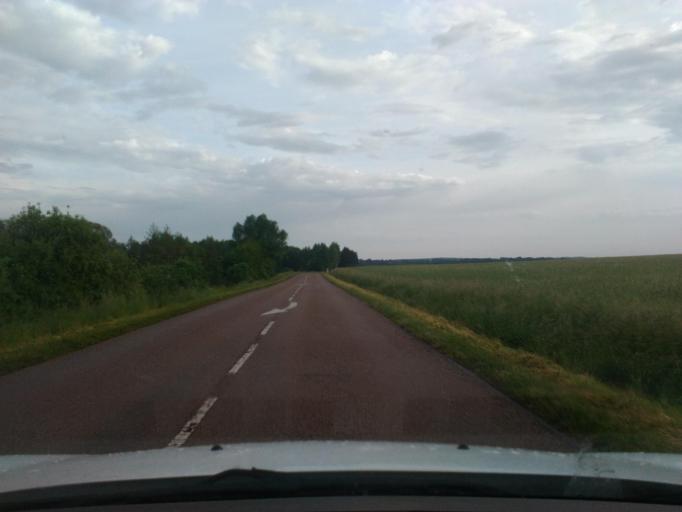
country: FR
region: Lorraine
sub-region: Departement des Vosges
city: Rambervillers
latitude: 48.4090
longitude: 6.5868
